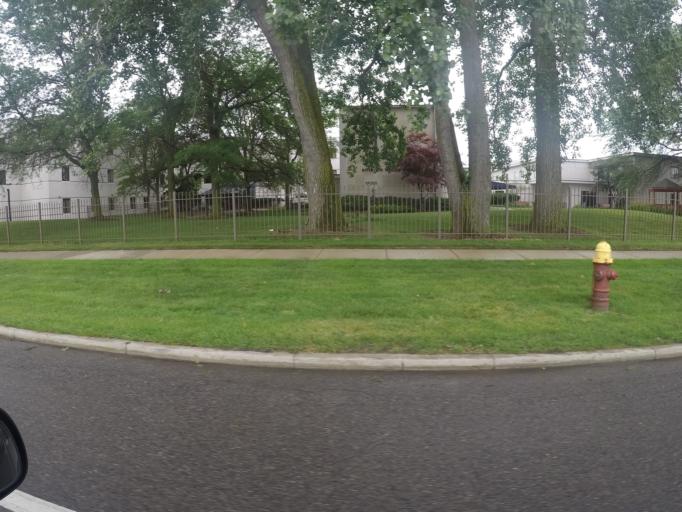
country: US
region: Michigan
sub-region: Wayne County
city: Harper Woods
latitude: 42.4111
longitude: -82.9161
